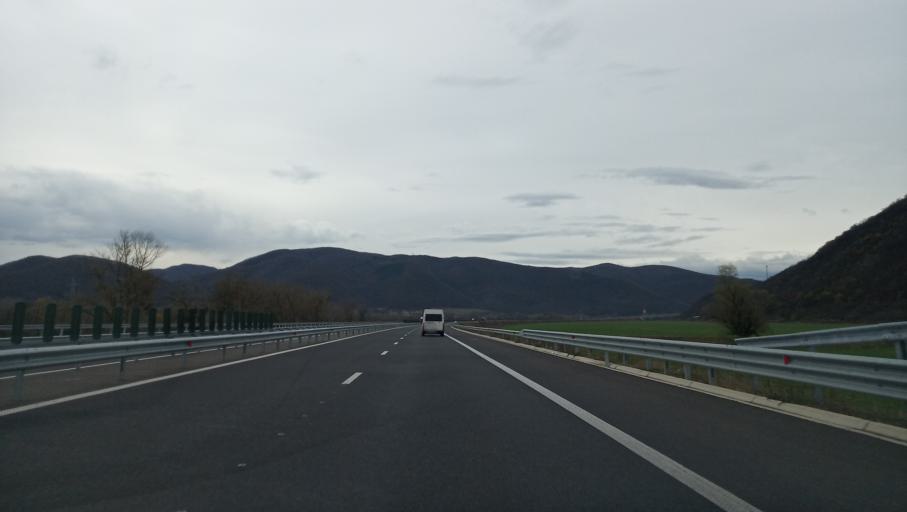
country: RO
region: Hunedoara
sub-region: Comuna Vetel
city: Vetel
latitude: 45.9171
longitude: 22.8146
